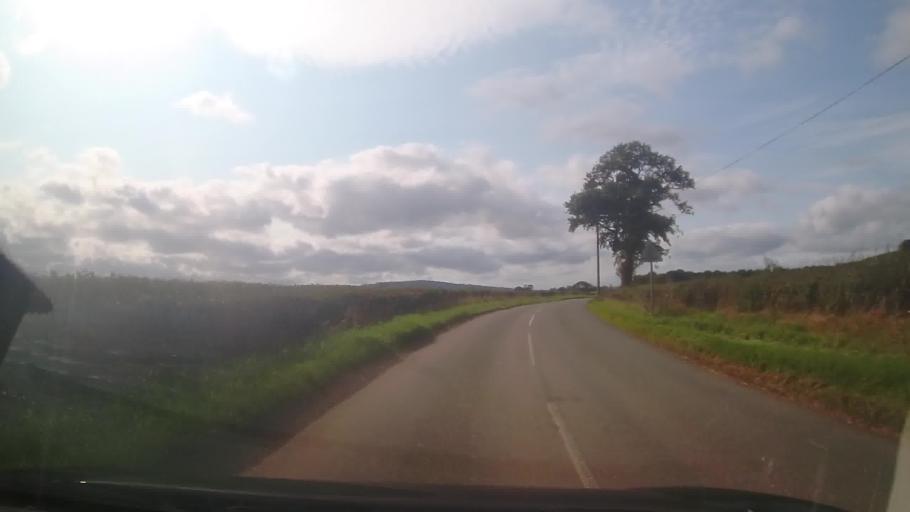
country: GB
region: England
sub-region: Shropshire
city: Norbury
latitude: 52.5161
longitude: -2.9496
